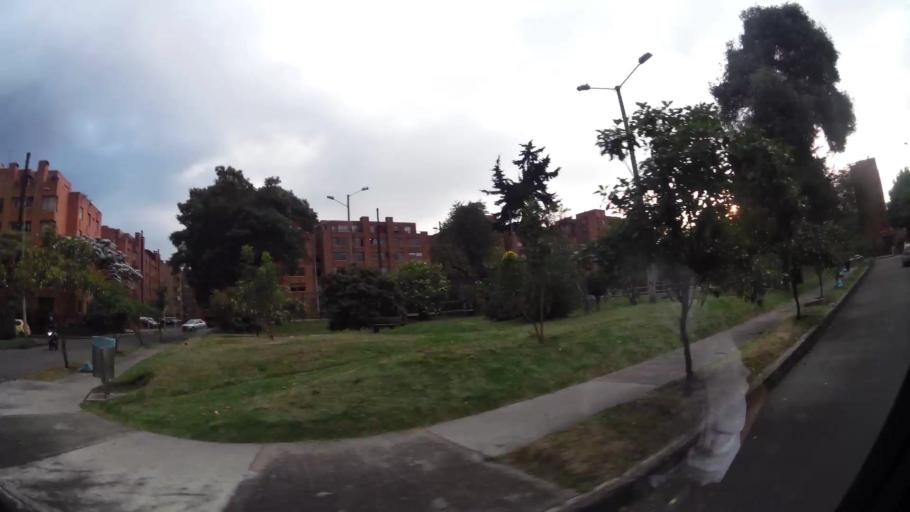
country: CO
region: Bogota D.C.
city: Barrio San Luis
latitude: 4.7263
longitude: -74.0662
